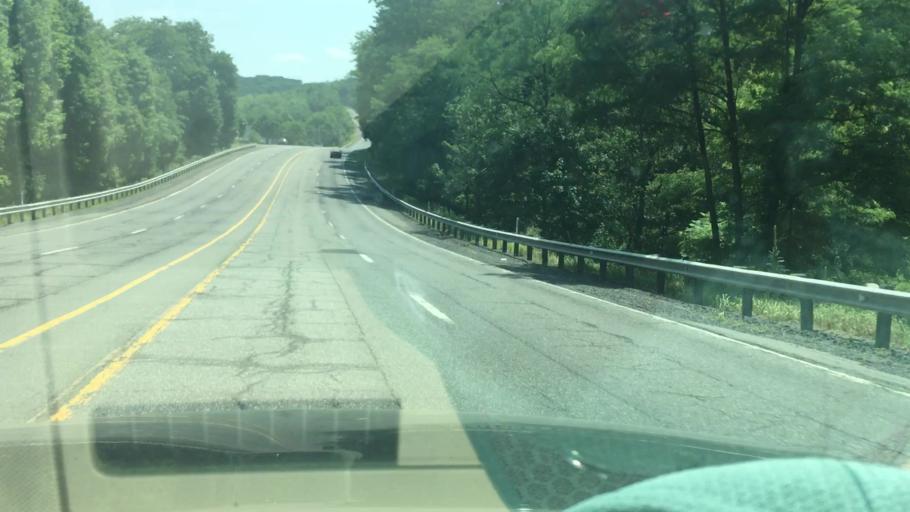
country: US
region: Pennsylvania
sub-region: Schuylkill County
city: Tamaqua
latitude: 40.7548
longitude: -75.9210
